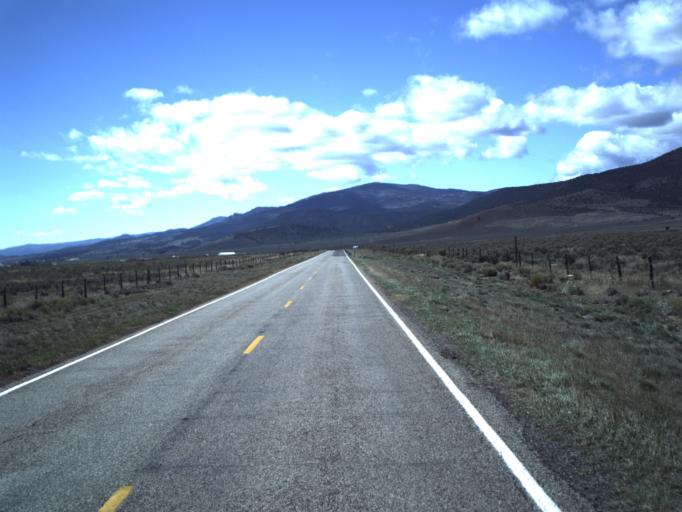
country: US
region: Utah
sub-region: Wayne County
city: Loa
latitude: 38.4803
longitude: -111.8957
